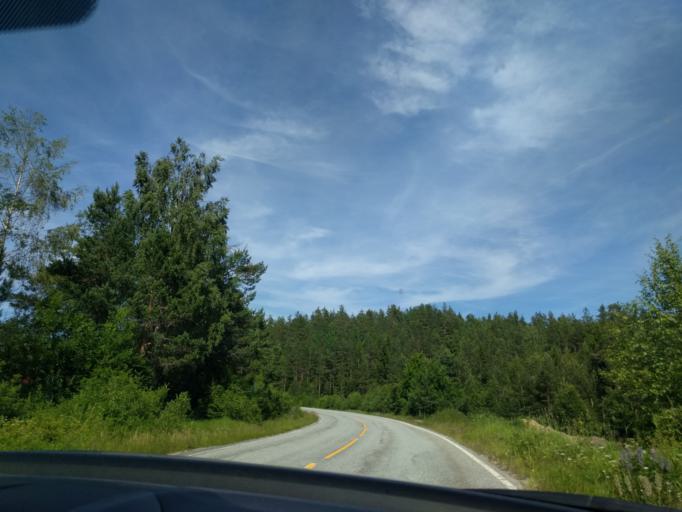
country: NO
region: Aust-Agder
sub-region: Gjerstad
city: Gjerstad
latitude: 58.8592
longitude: 9.1398
